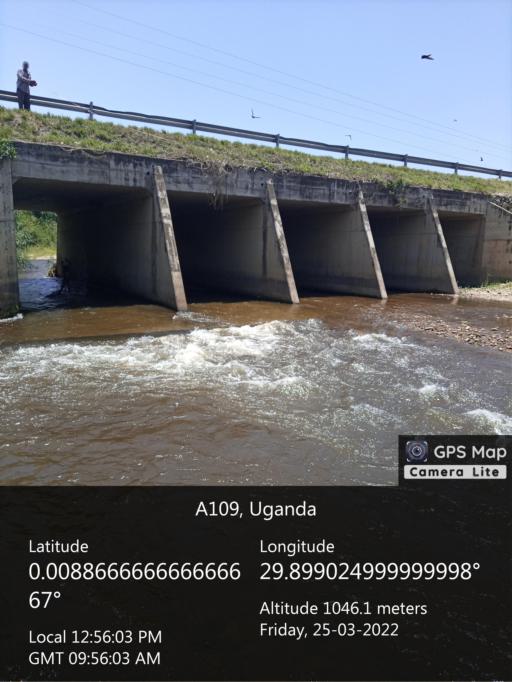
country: UG
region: Western Region
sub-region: Kasese District
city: Kilembe
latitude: 0.0089
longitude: 29.8990
